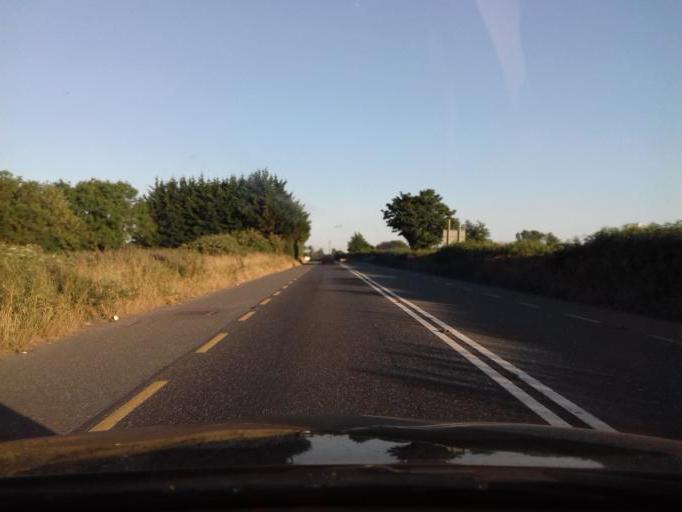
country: IE
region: Leinster
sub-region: Fingal County
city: Blanchardstown
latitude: 53.4429
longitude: -6.3402
